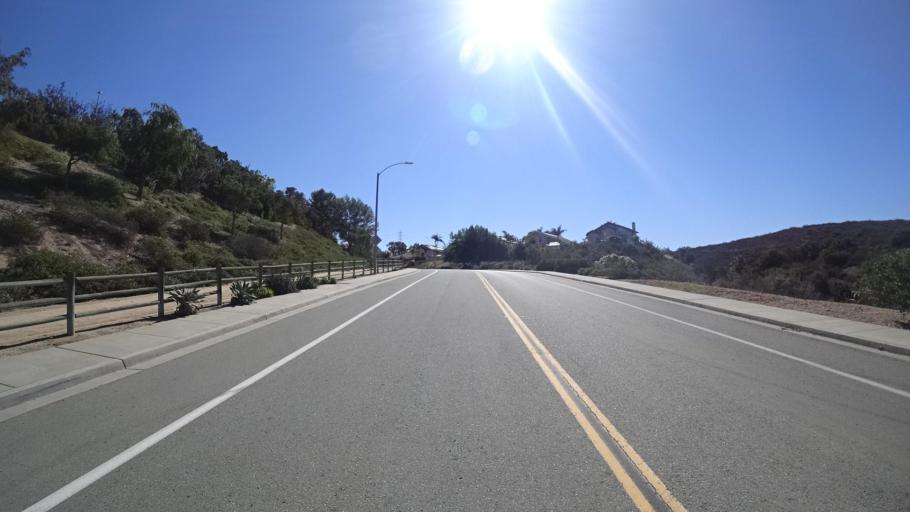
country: US
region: California
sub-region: San Diego County
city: La Presa
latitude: 32.6647
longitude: -116.9793
